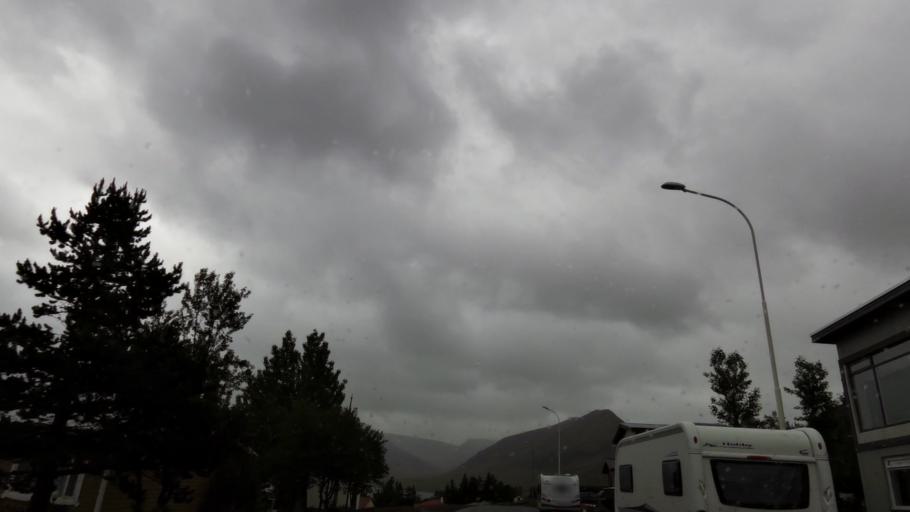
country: IS
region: Westfjords
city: Isafjoerdur
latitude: 65.8722
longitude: -23.4837
